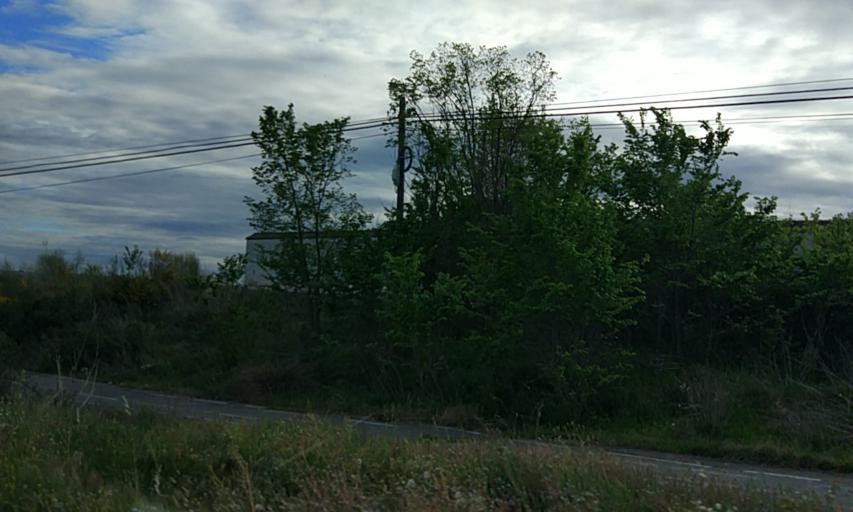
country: ES
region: Extremadura
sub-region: Provincia de Caceres
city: Coria
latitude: 40.0008
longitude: -6.5507
